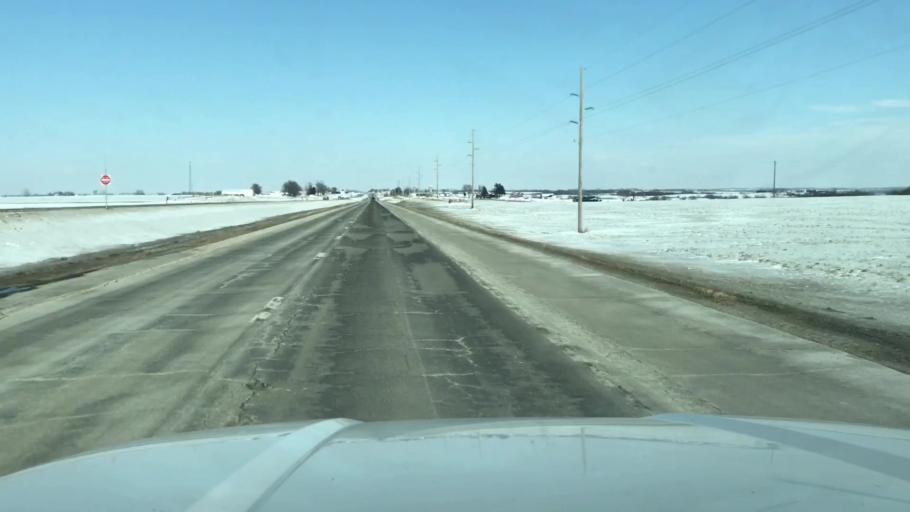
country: US
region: Missouri
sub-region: Nodaway County
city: Maryville
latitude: 40.2297
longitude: -94.8677
